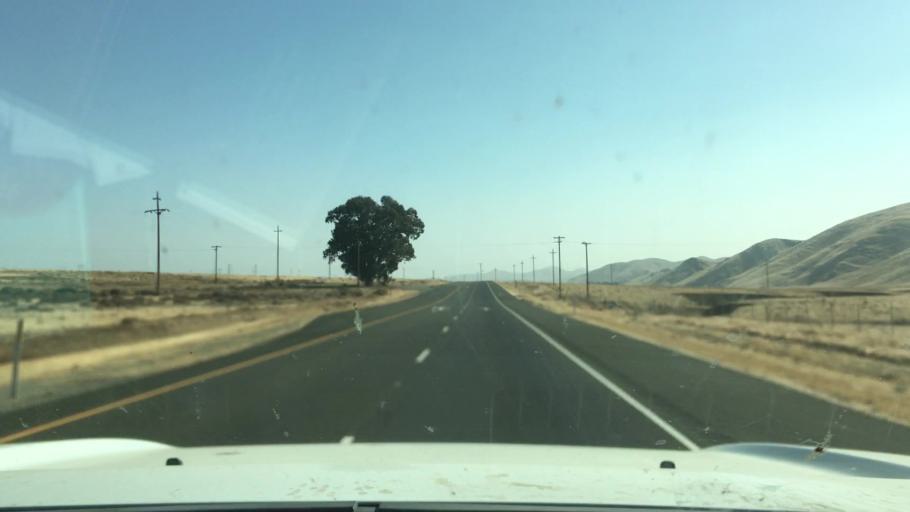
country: US
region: California
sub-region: San Luis Obispo County
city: Shandon
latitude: 35.7122
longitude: -120.1671
